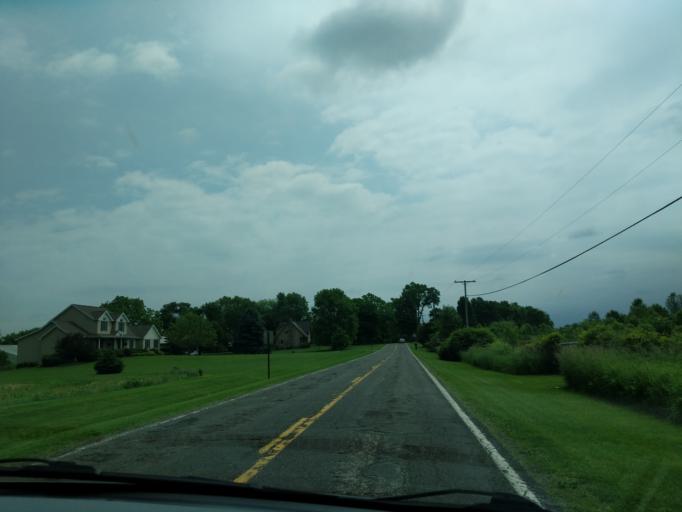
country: US
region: Michigan
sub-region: Ingham County
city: Williamston
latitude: 42.6938
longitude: -84.2614
